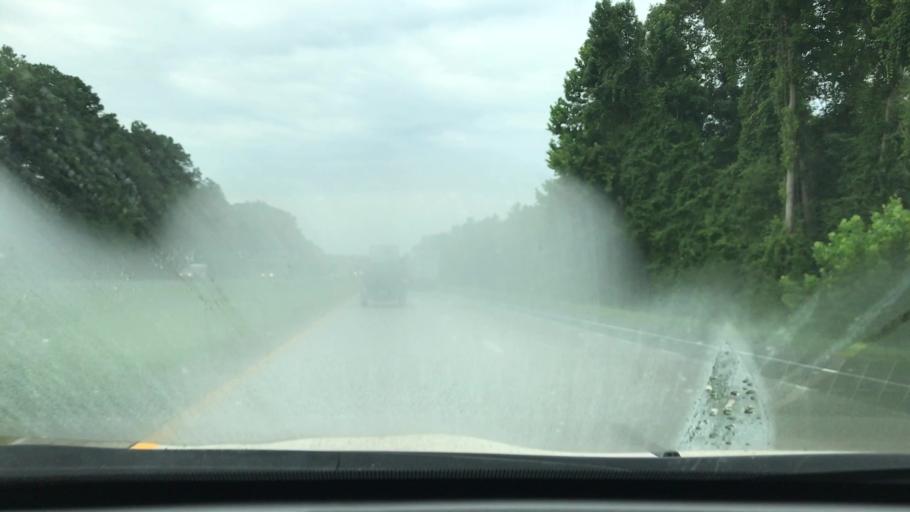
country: US
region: South Carolina
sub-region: Jasper County
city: Ridgeland
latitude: 32.4719
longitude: -80.9745
